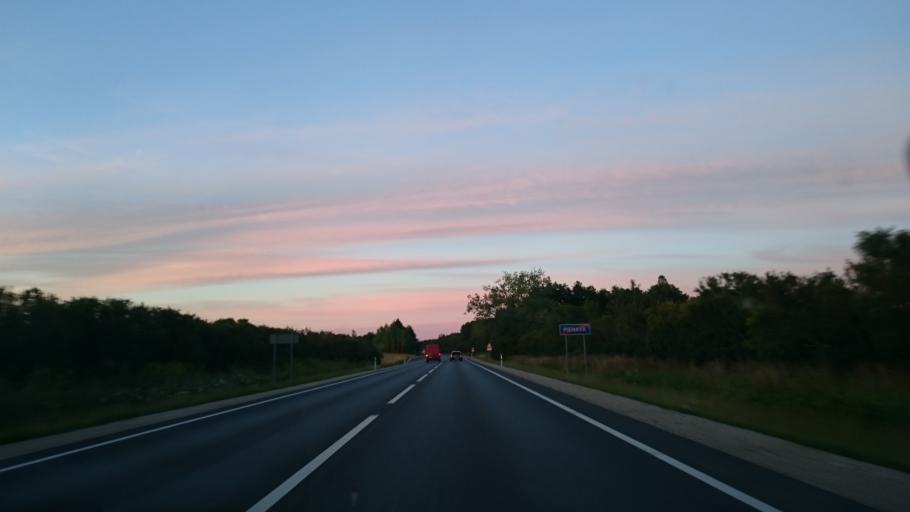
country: LV
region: Dobeles Rajons
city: Dobele
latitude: 56.7457
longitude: 23.2573
